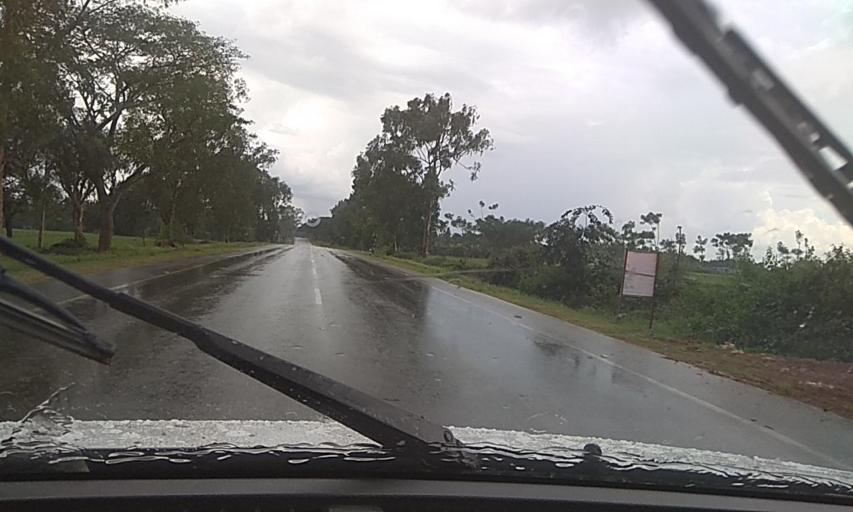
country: IN
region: Karnataka
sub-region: Tumkur
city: Kunigal
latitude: 12.9463
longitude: 77.0276
